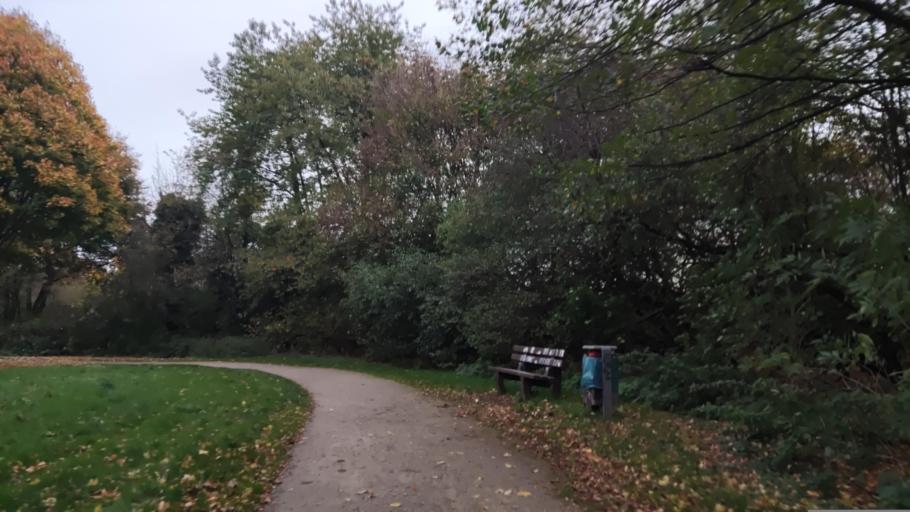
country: DE
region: North Rhine-Westphalia
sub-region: Regierungsbezirk Arnsberg
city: Herne
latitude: 51.5574
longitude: 7.2138
